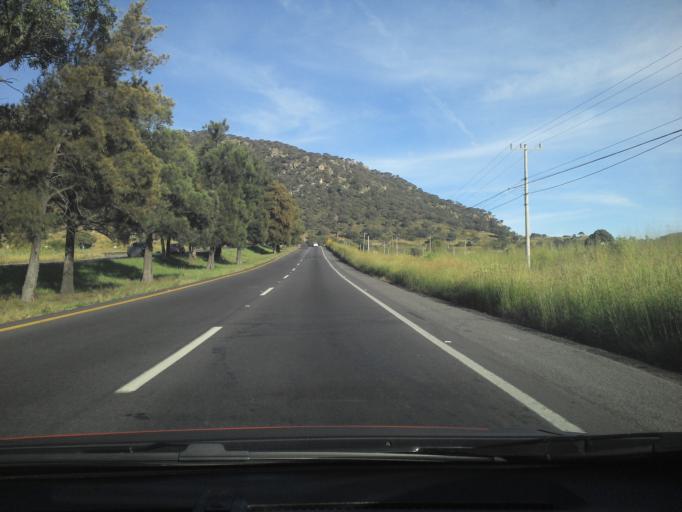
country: MX
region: Jalisco
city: La Venta del Astillero
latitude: 20.7364
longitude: -103.5837
